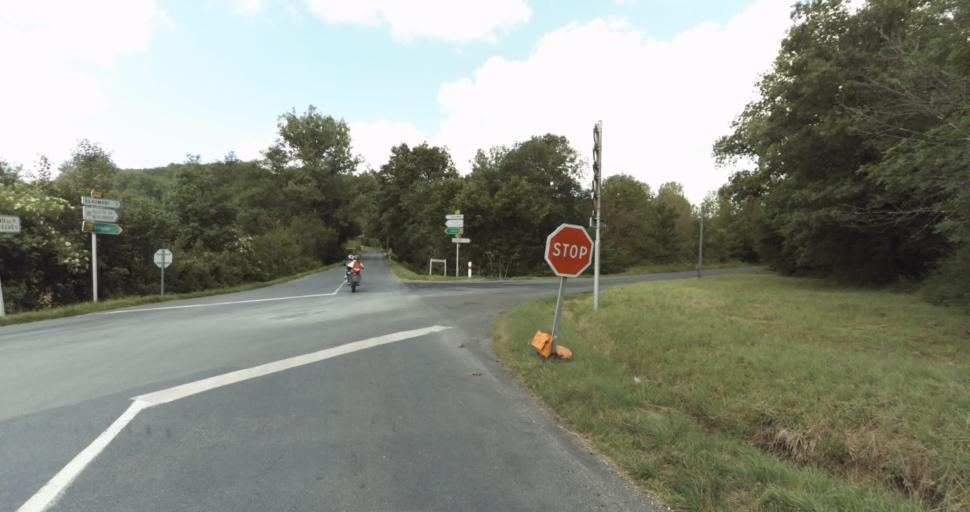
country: FR
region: Aquitaine
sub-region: Departement de la Dordogne
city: Beaumont-du-Perigord
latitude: 44.7705
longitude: 0.7998
